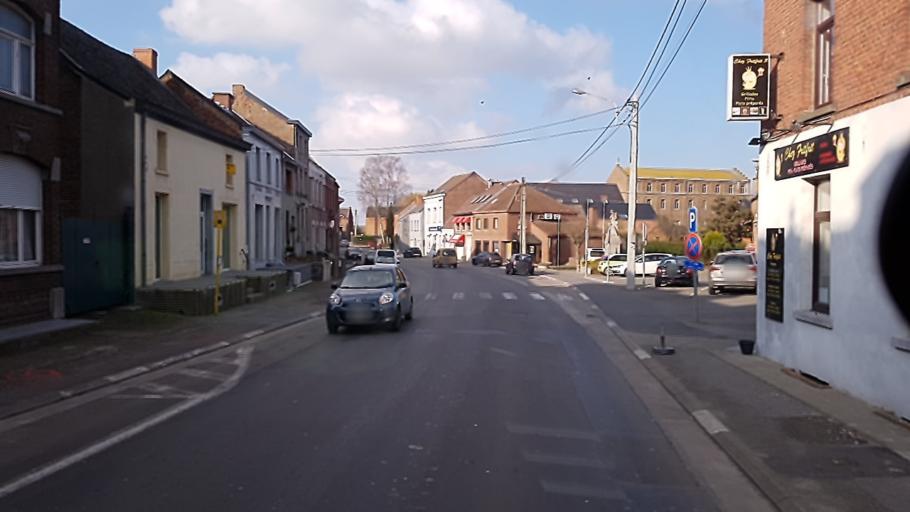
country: BE
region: Wallonia
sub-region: Province du Hainaut
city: Estinnes-au-Val
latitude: 50.3793
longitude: 4.0298
